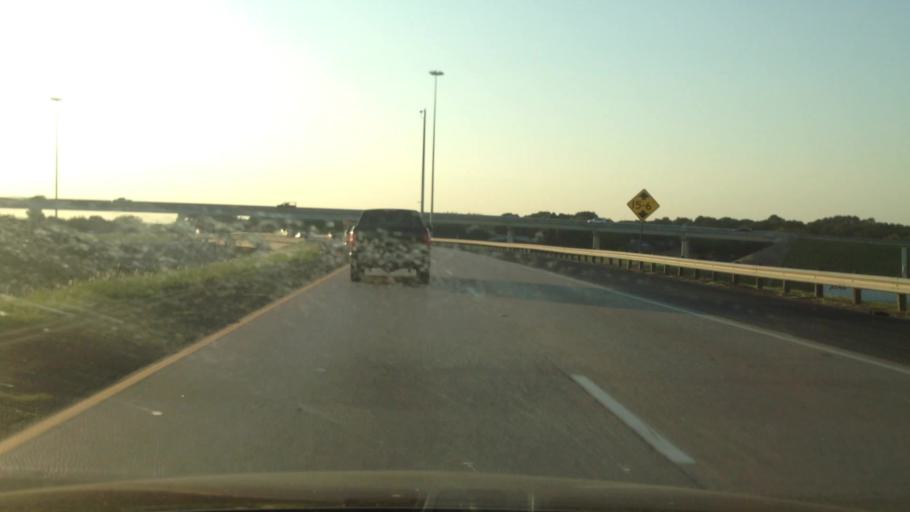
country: US
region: Texas
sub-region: Tarrant County
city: Kennedale
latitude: 32.6697
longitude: -97.2060
